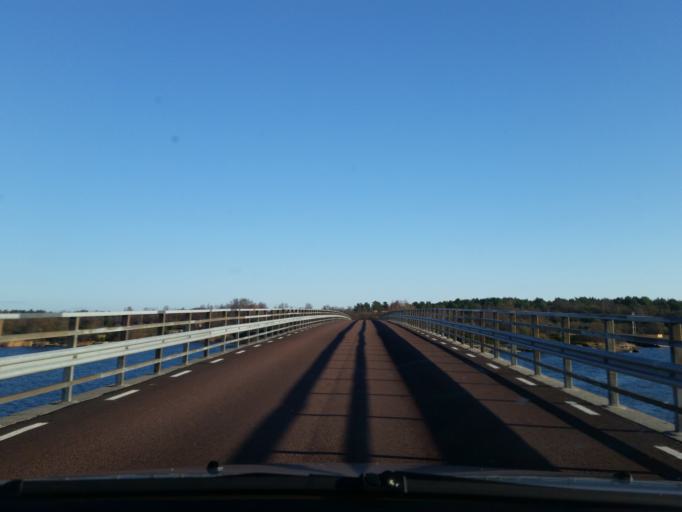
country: AX
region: Alands skaergard
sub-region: Braendoe
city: Braendoe
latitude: 60.4456
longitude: 21.0620
